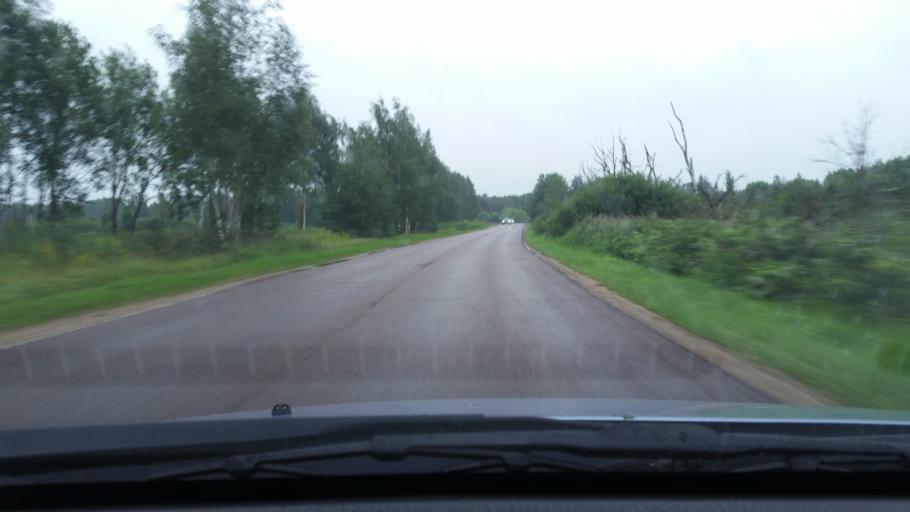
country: LV
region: Riga
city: Bolderaja
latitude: 56.9911
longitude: 24.0315
